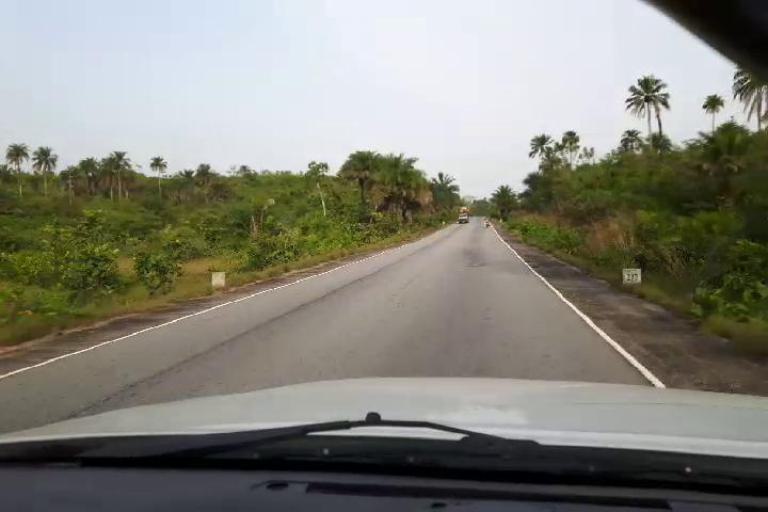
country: SL
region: Eastern Province
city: Blama
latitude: 7.9026
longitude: -11.4013
